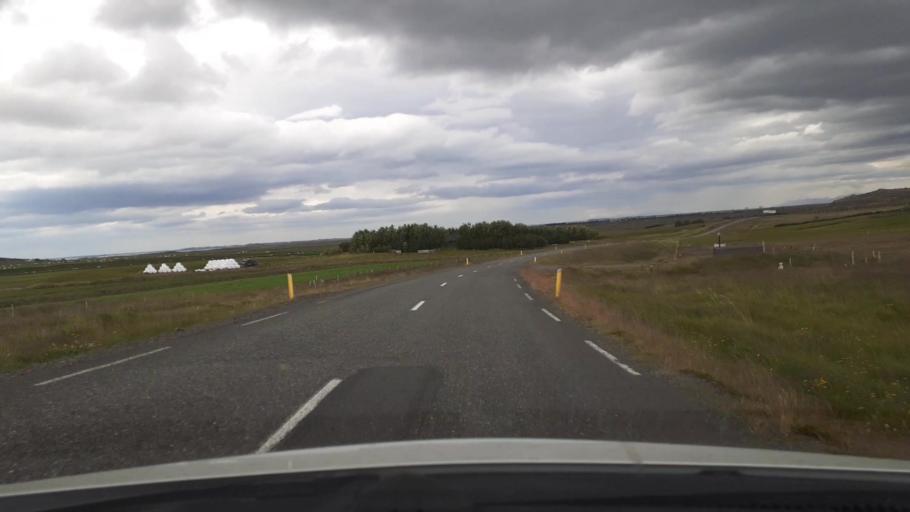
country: IS
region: West
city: Borgarnes
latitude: 64.5455
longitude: -21.6899
